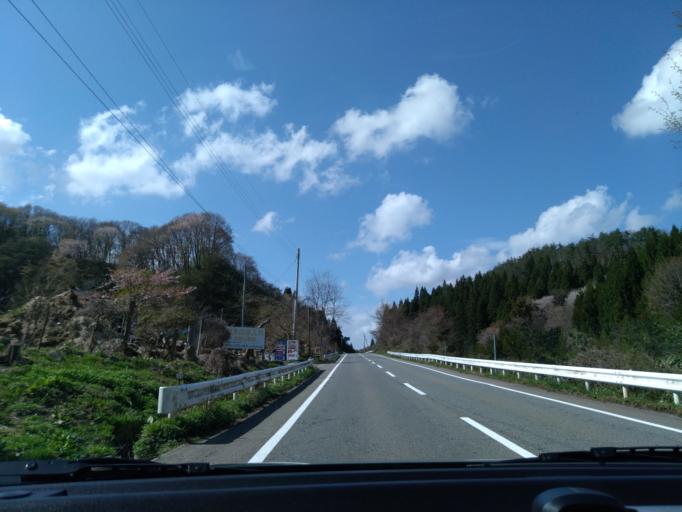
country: JP
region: Akita
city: Akita
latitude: 39.6937
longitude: 140.2222
